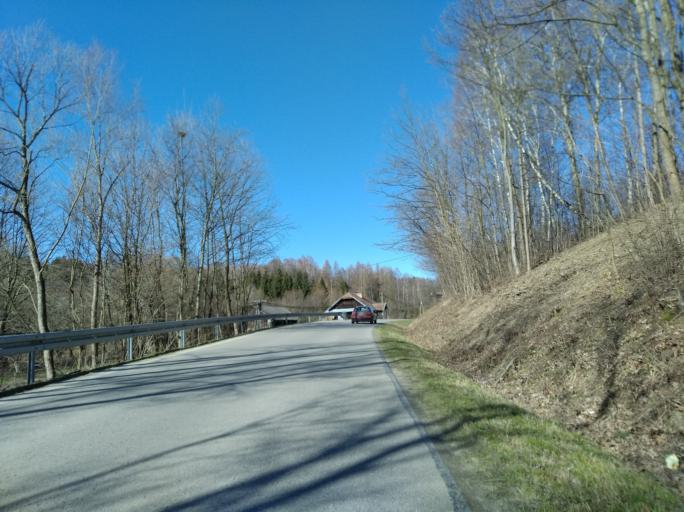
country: PL
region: Subcarpathian Voivodeship
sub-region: Powiat strzyzowski
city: Wisniowa
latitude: 49.8907
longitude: 21.6653
